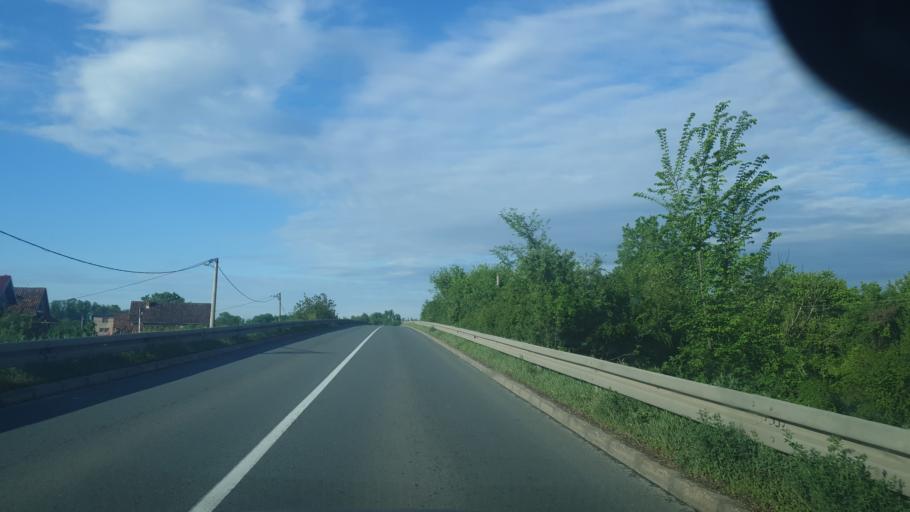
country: RS
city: Zvecka
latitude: 44.6099
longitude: 20.1566
